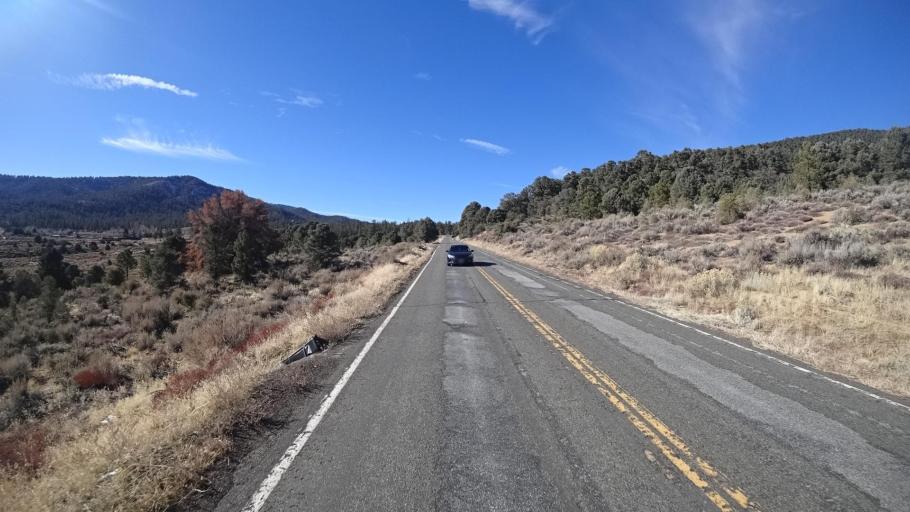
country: US
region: California
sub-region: Kern County
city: Pine Mountain Club
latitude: 34.8437
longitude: -119.0687
